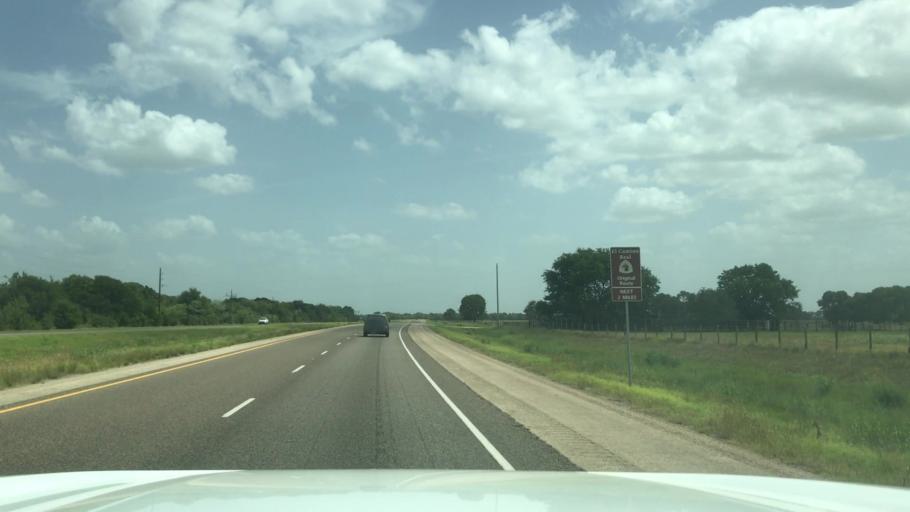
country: US
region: Texas
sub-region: Robertson County
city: Calvert
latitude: 31.0015
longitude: -96.6954
